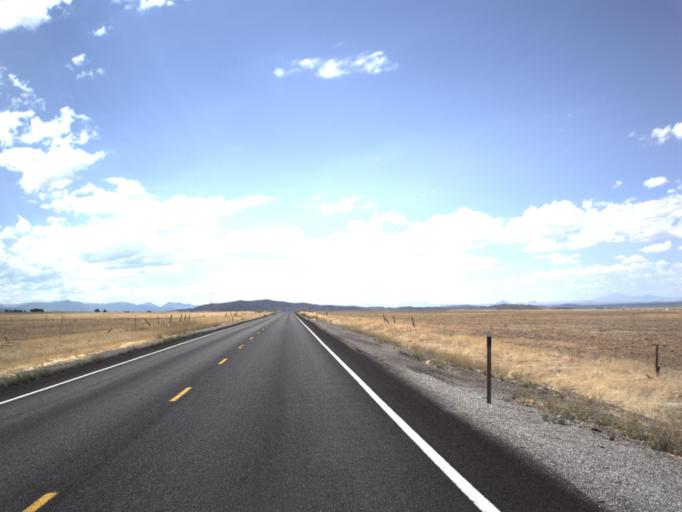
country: US
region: Utah
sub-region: Millard County
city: Fillmore
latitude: 39.1252
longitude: -112.2549
